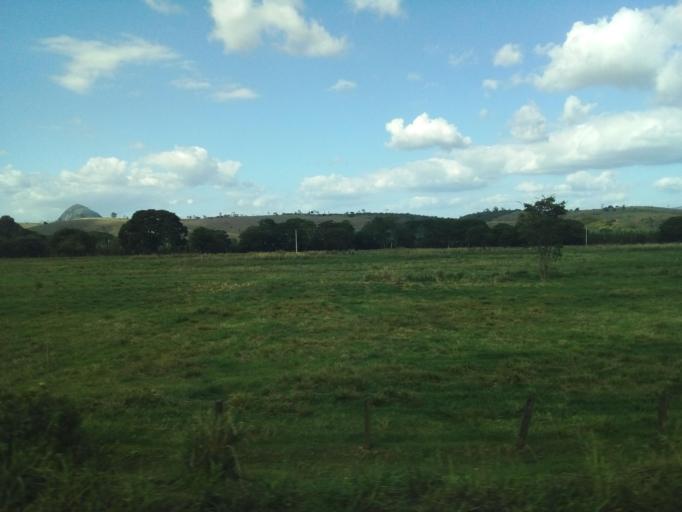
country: BR
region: Minas Gerais
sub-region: Conselheiro Pena
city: Conselheiro Pena
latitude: -18.9966
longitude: -41.5937
